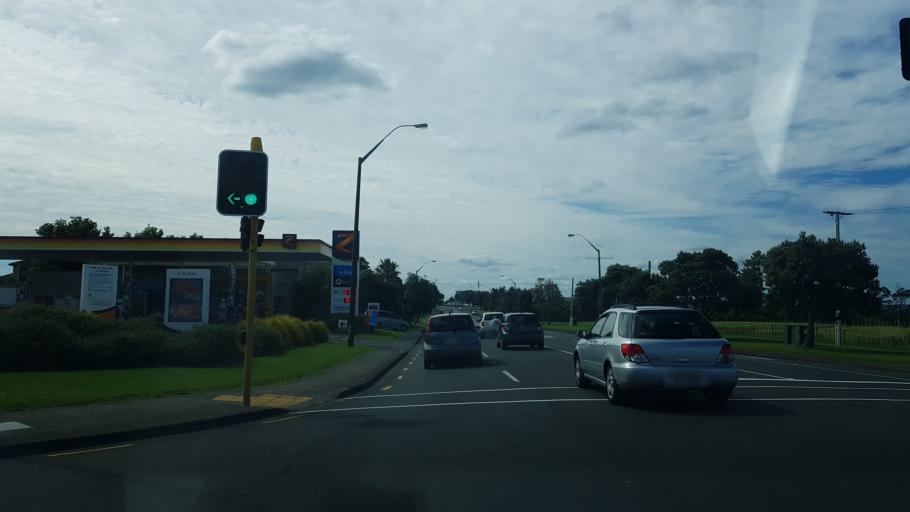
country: NZ
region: Auckland
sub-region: Auckland
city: Rosebank
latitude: -36.8508
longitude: 174.6511
